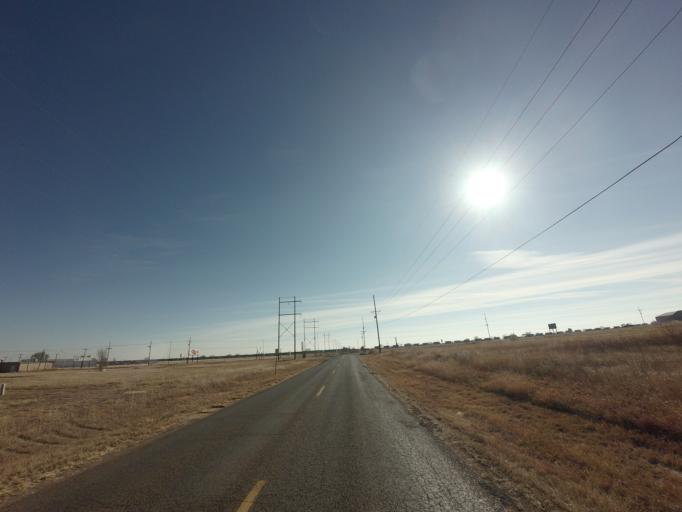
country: US
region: New Mexico
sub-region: Curry County
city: Clovis
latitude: 34.4058
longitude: -103.2494
